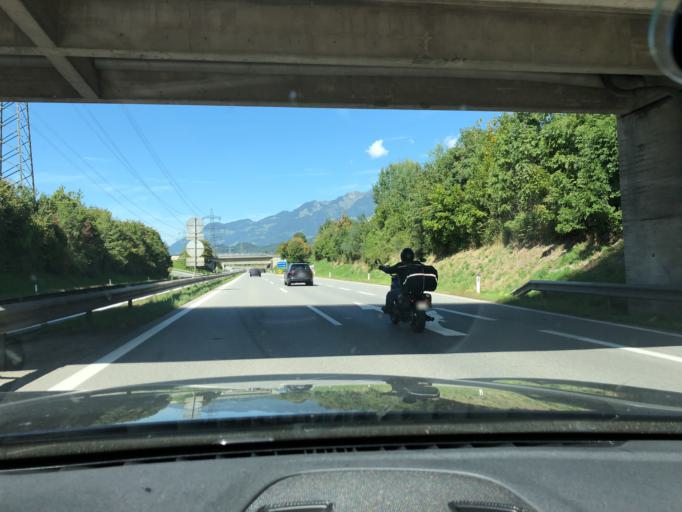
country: AT
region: Vorarlberg
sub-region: Politischer Bezirk Bludenz
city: Bludenz
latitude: 47.1486
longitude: 9.8168
